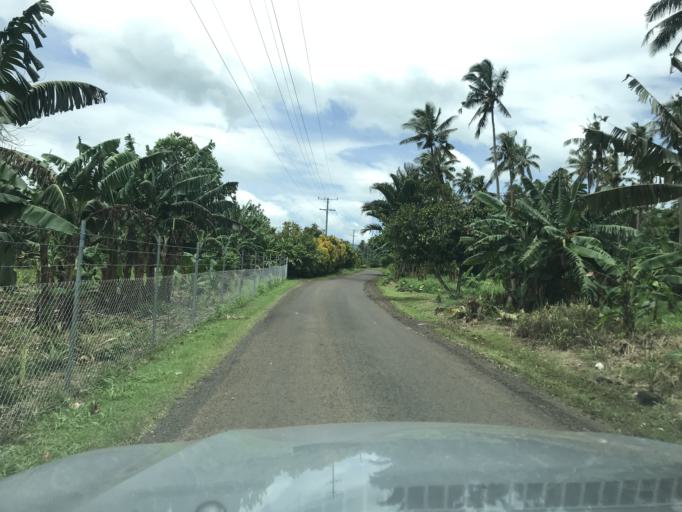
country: WS
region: Tuamasaga
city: Afenga
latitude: -13.8103
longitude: -171.8854
